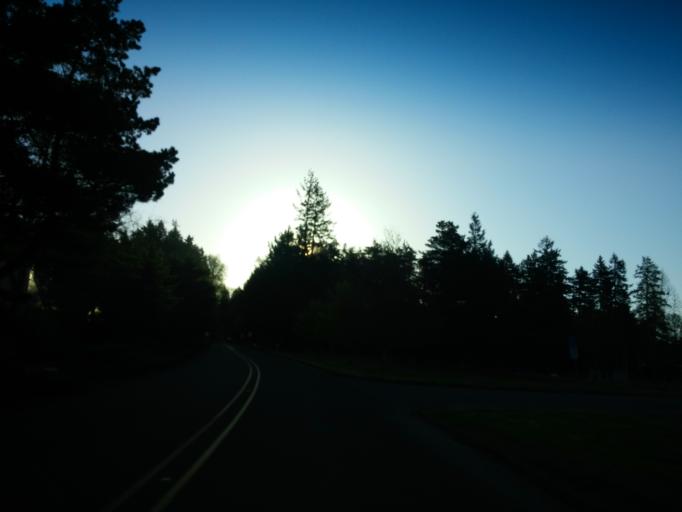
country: US
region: Oregon
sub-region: Washington County
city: Cedar Hills
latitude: 45.5070
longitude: -122.7920
